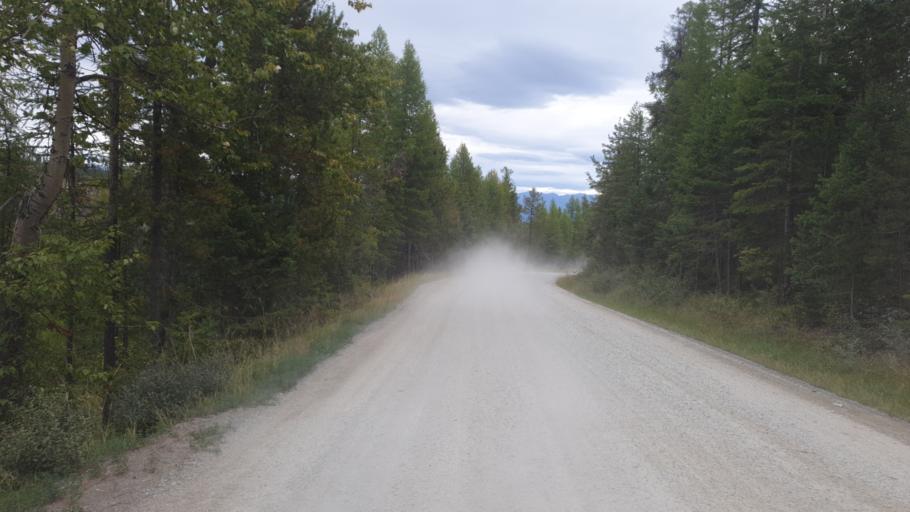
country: US
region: Montana
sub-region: Flathead County
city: Lakeside
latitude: 47.9924
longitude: -114.3297
